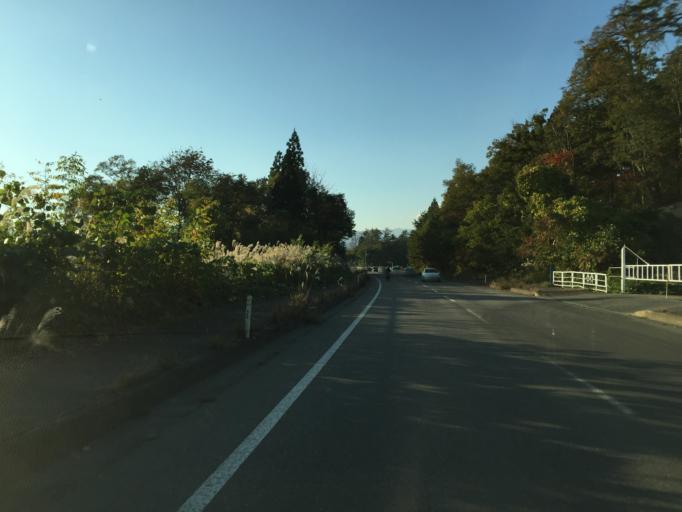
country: JP
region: Fukushima
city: Kitakata
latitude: 37.6956
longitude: 139.8876
